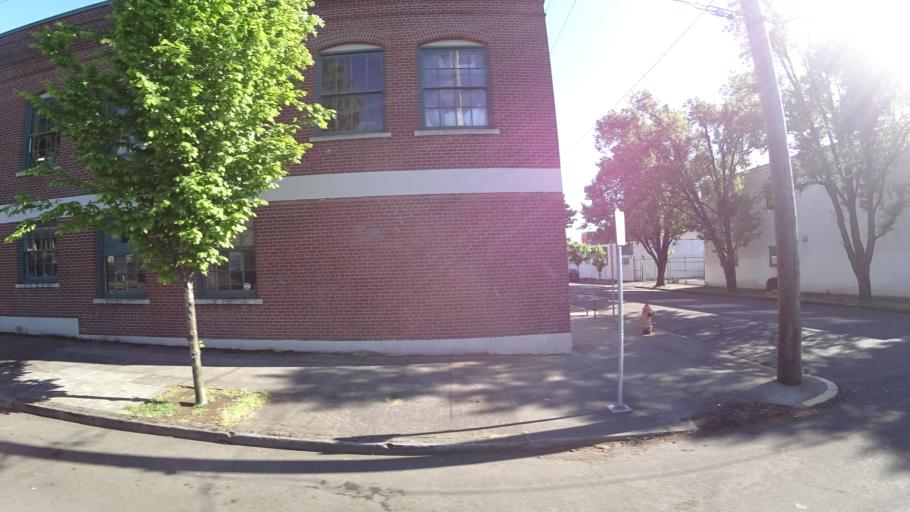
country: US
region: Oregon
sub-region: Multnomah County
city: Portland
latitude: 45.5250
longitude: -122.6586
